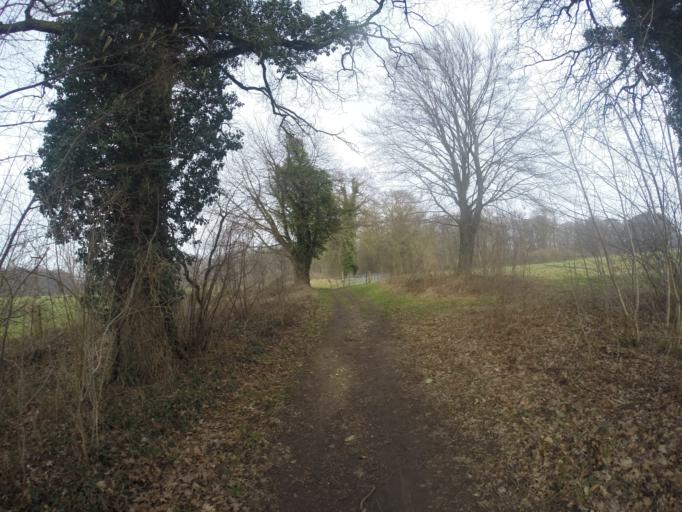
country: NL
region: Gelderland
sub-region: Gemeente Bronckhorst
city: Hengelo
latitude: 52.0933
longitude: 6.2878
